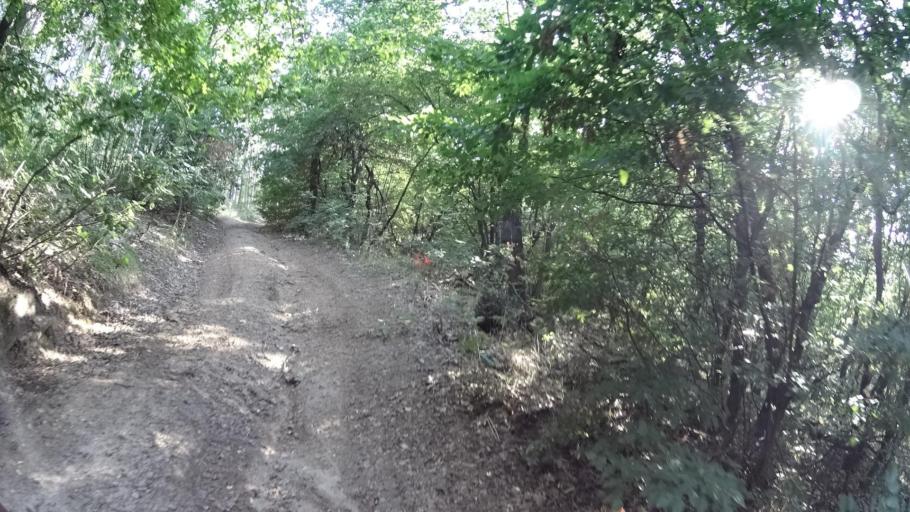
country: BG
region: Plovdiv
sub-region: Obshtina Plovdiv
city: Plovdiv
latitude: 42.0591
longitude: 24.6869
